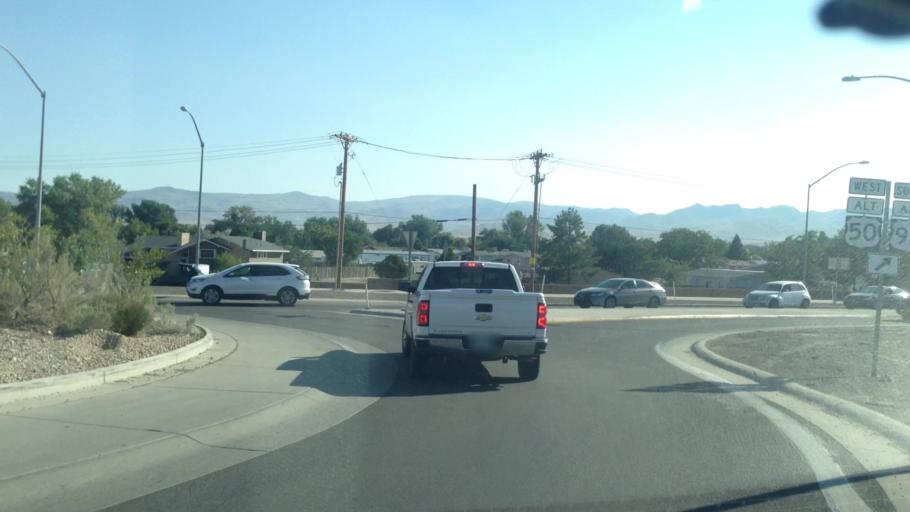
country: US
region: Nevada
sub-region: Lyon County
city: Fernley
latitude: 39.6038
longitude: -119.2272
